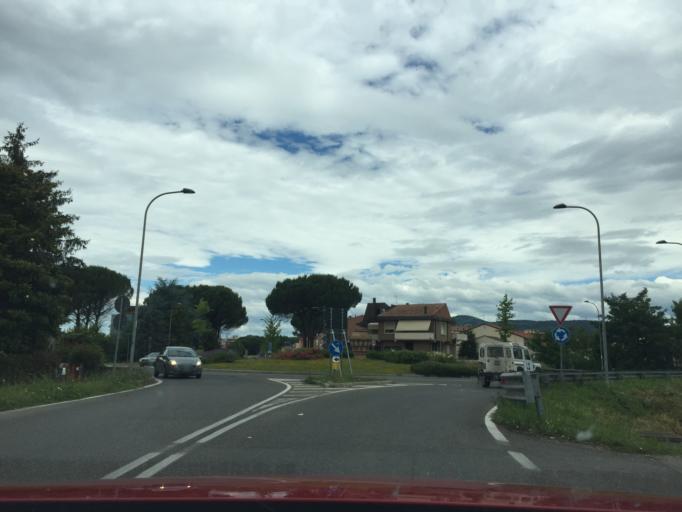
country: IT
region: Tuscany
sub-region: Province of Florence
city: Montelupo Fiorentino
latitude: 43.7283
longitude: 11.0224
